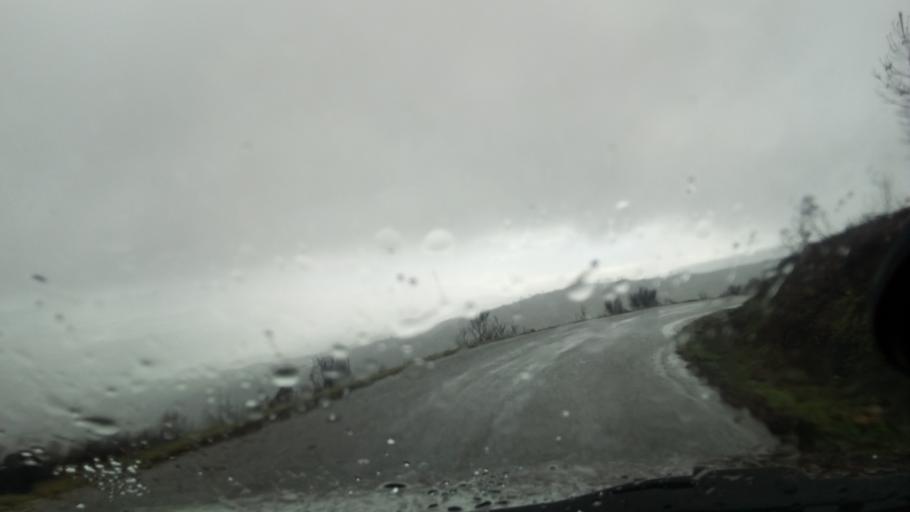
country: PT
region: Guarda
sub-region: Celorico da Beira
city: Celorico da Beira
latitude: 40.5405
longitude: -7.4465
